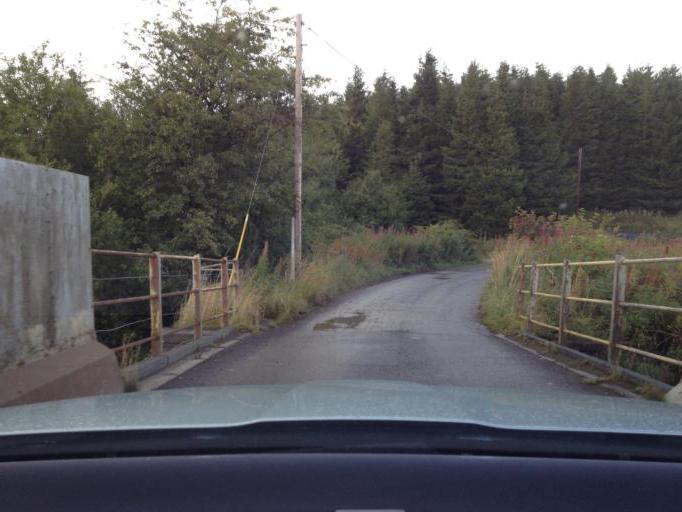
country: GB
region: Scotland
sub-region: West Lothian
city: West Calder
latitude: 55.8033
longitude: -3.5781
